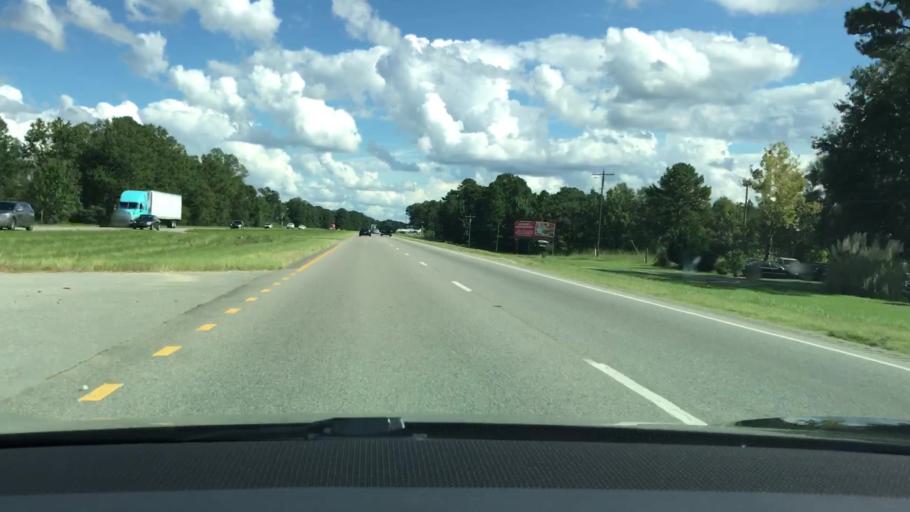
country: US
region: Alabama
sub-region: Montgomery County
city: Taylor
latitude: 32.0490
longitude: -86.0411
